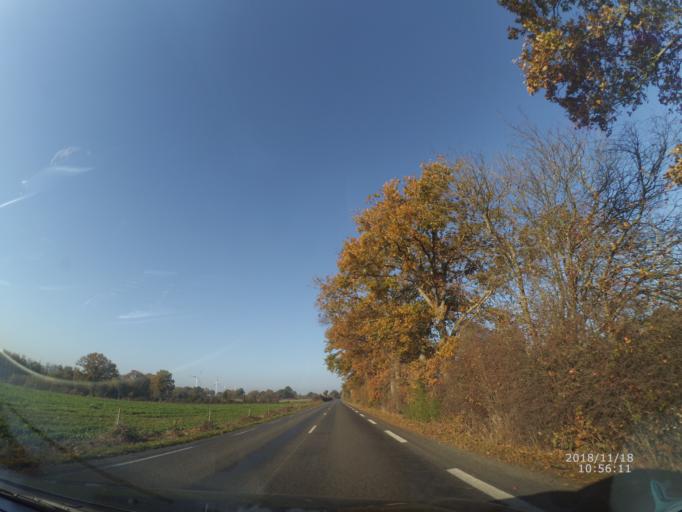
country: FR
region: Pays de la Loire
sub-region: Departement de la Loire-Atlantique
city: Chauve
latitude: 47.1874
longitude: -1.9803
